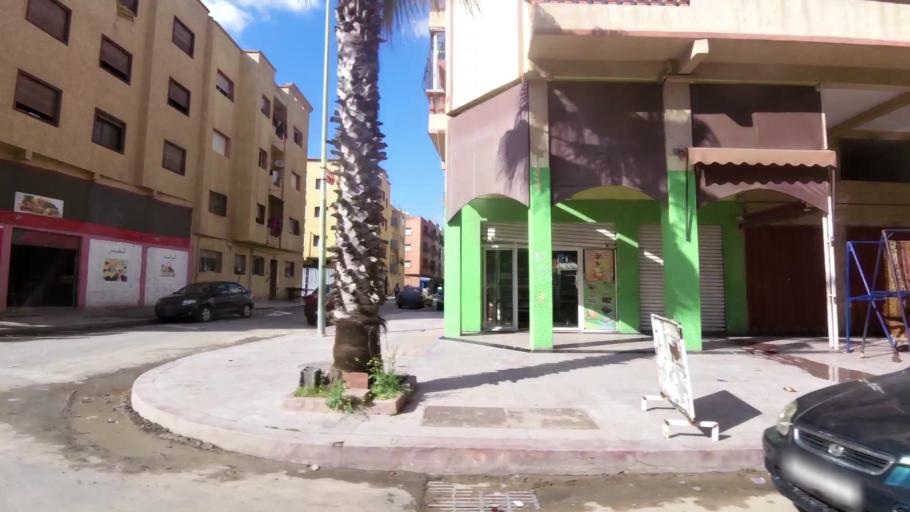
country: MA
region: Chaouia-Ouardigha
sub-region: Settat Province
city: Berrechid
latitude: 33.2745
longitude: -7.5787
